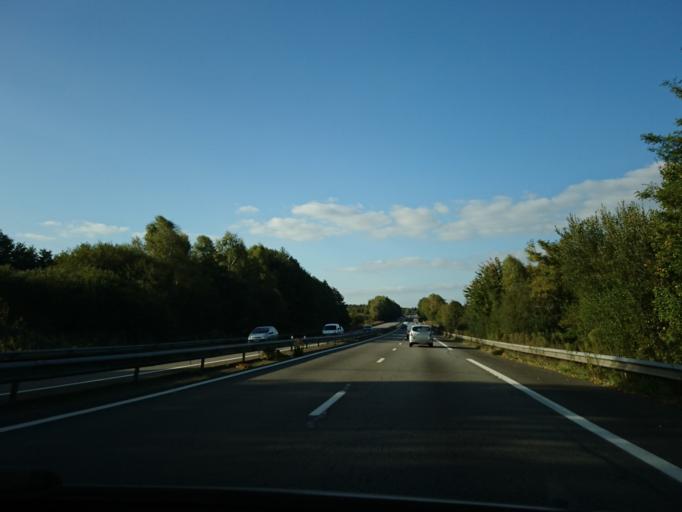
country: FR
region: Pays de la Loire
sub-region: Departement de la Loire-Atlantique
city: Treillieres
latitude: 47.3225
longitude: -1.6458
